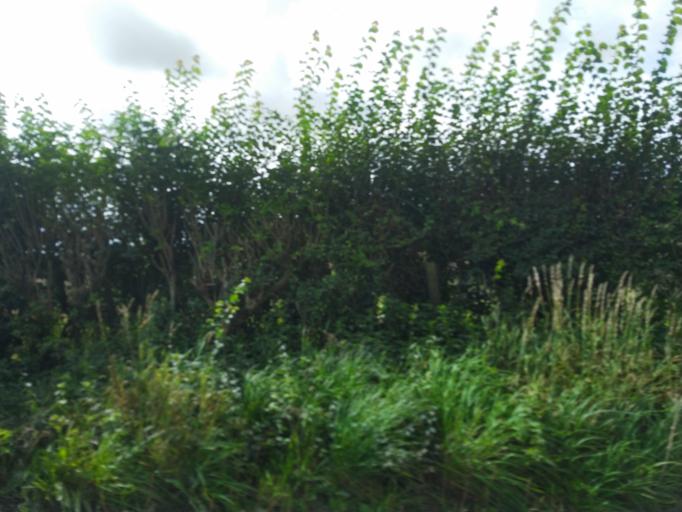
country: GB
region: England
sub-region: Dorset
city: Lytchett Matravers
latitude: 50.7943
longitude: -2.1147
